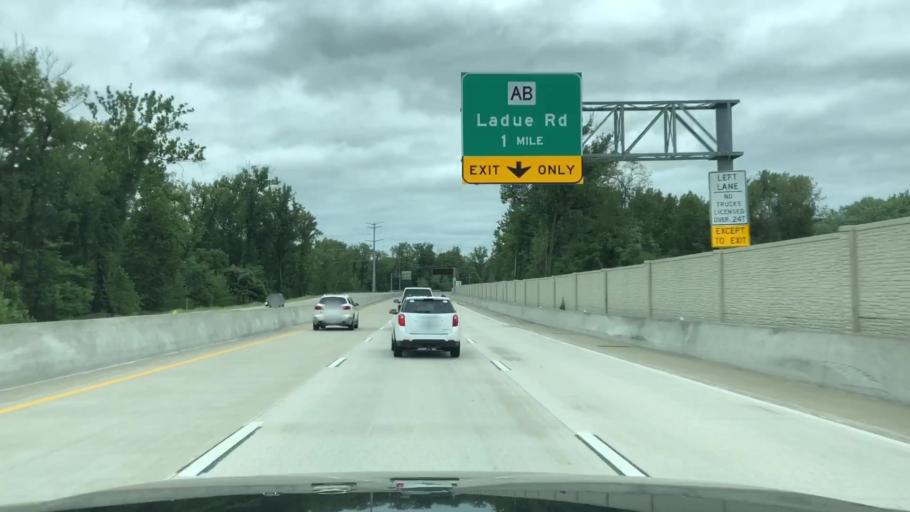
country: US
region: Missouri
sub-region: Saint Louis County
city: Town and Country
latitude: 38.6746
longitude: -90.4938
